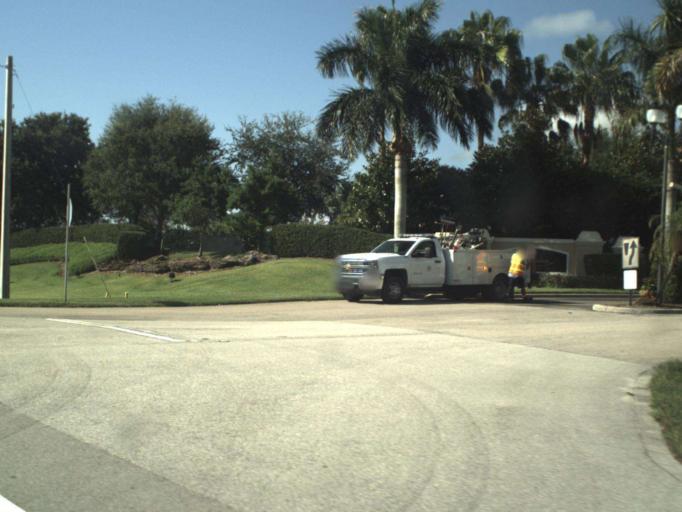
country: US
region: Florida
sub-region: Indian River County
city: Gifford
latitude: 27.6705
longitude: -80.3972
